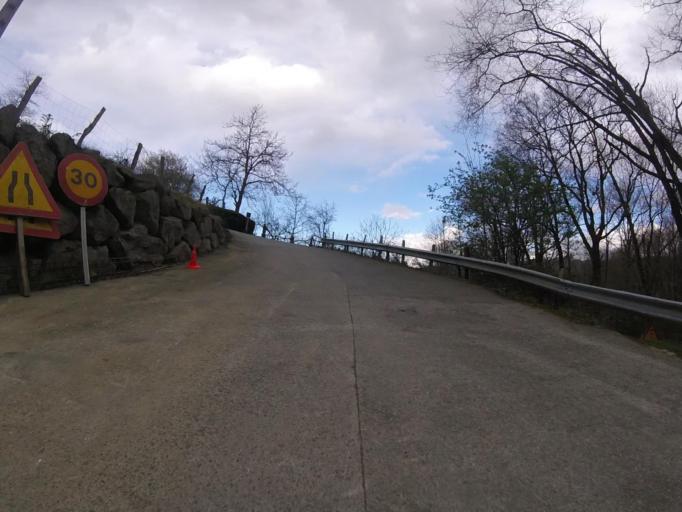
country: ES
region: Basque Country
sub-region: Provincia de Guipuzcoa
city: Errenteria
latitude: 43.2808
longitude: -1.8564
